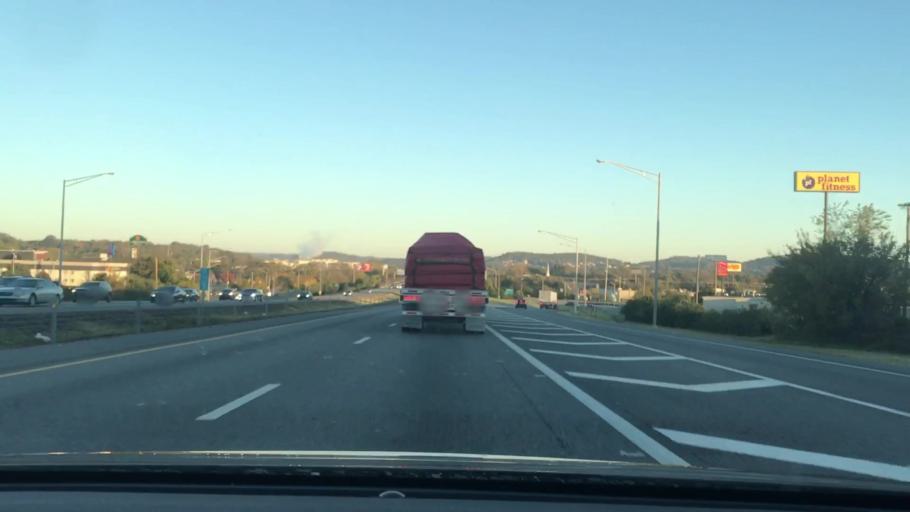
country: US
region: Tennessee
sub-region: Davidson County
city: Goodlettsville
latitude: 36.3204
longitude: -86.7032
